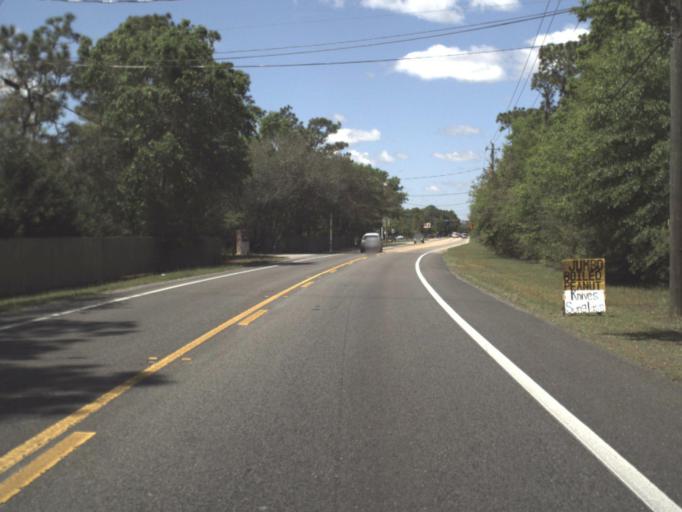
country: US
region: Florida
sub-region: Escambia County
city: Myrtle Grove
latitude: 30.3977
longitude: -87.3963
